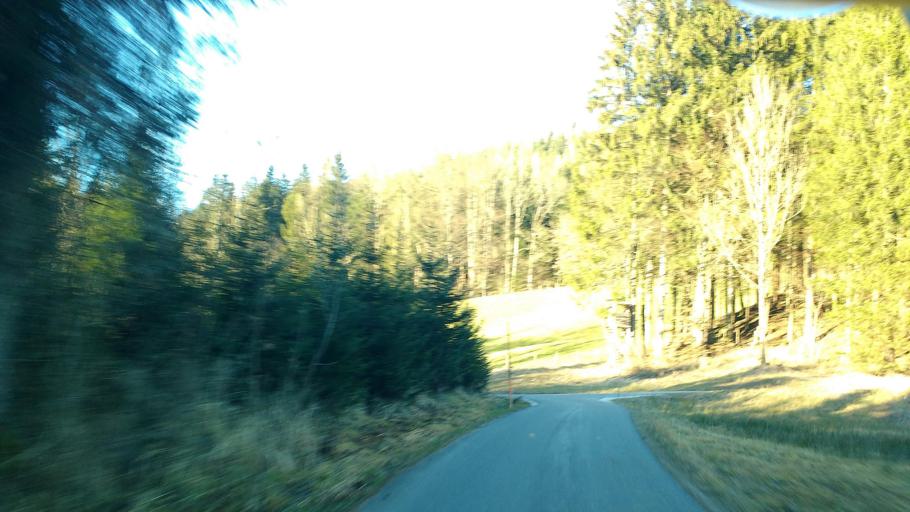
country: AT
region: Upper Austria
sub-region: Politischer Bezirk Kirchdorf an der Krems
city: Micheldorf in Oberoesterreich
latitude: 47.9031
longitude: 14.1781
